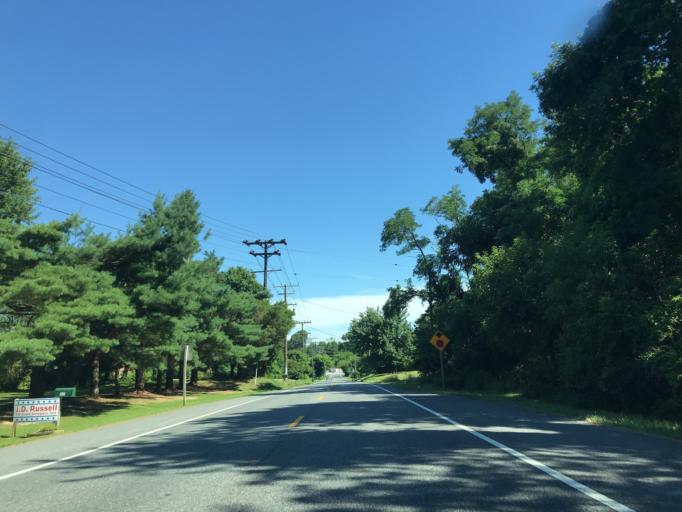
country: US
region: Maryland
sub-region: Harford County
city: Riverside
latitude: 39.4767
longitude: -76.2660
